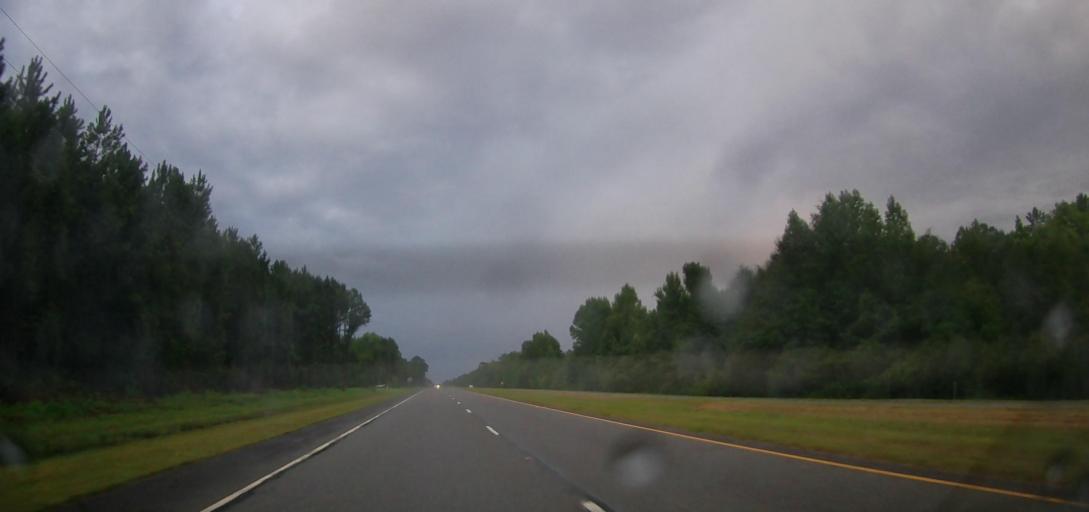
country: US
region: Georgia
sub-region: Lanier County
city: Lakeland
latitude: 30.9468
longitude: -82.9798
